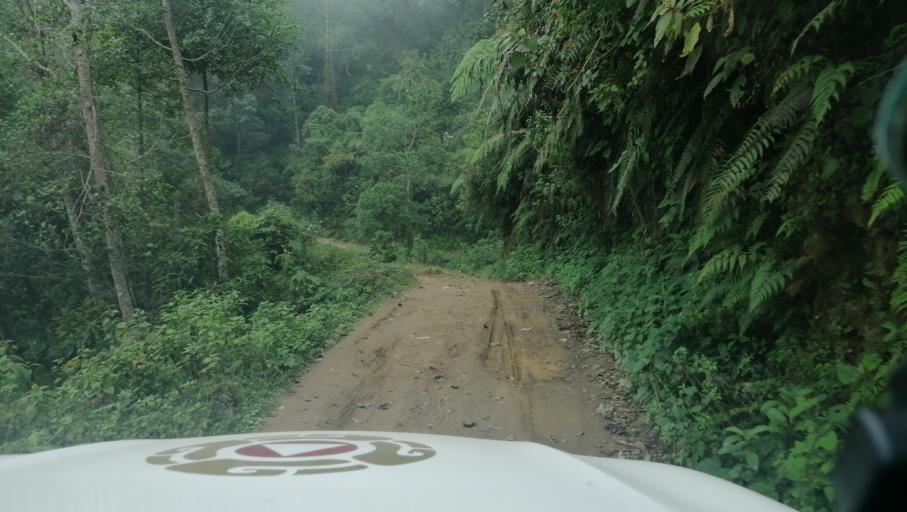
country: GT
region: San Marcos
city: Tacana
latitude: 15.2153
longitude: -92.1830
